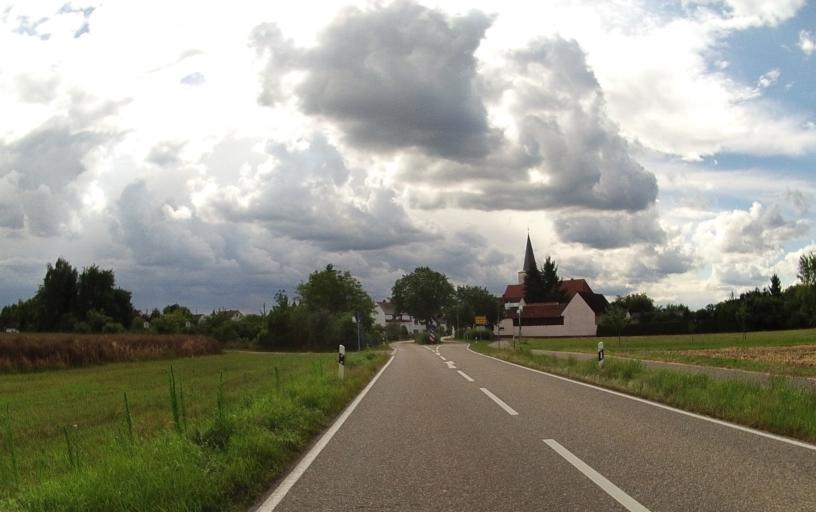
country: DE
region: Rheinland-Pfalz
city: Scheibenhardt
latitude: 48.9812
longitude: 8.1470
